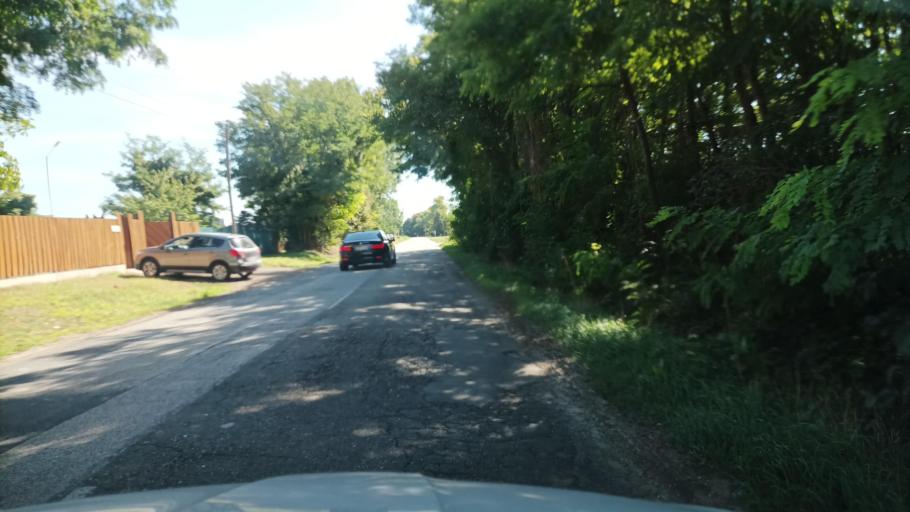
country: HU
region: Pest
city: Vacszentlaszlo
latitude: 47.5674
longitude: 19.5452
